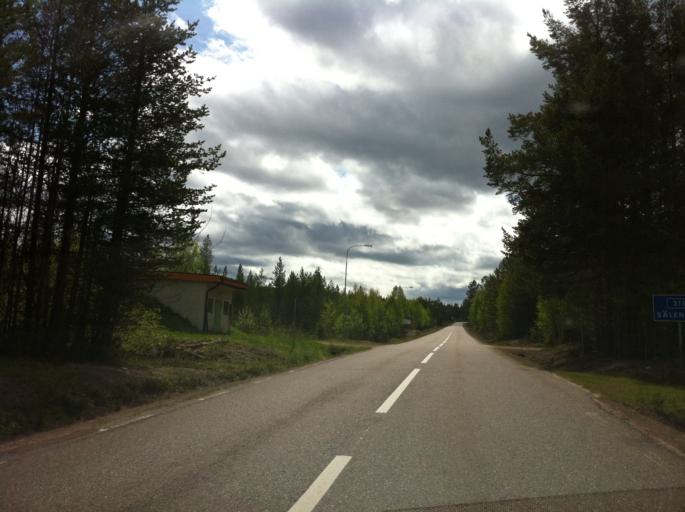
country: NO
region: Hedmark
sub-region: Trysil
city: Innbygda
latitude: 61.6859
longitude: 13.1291
